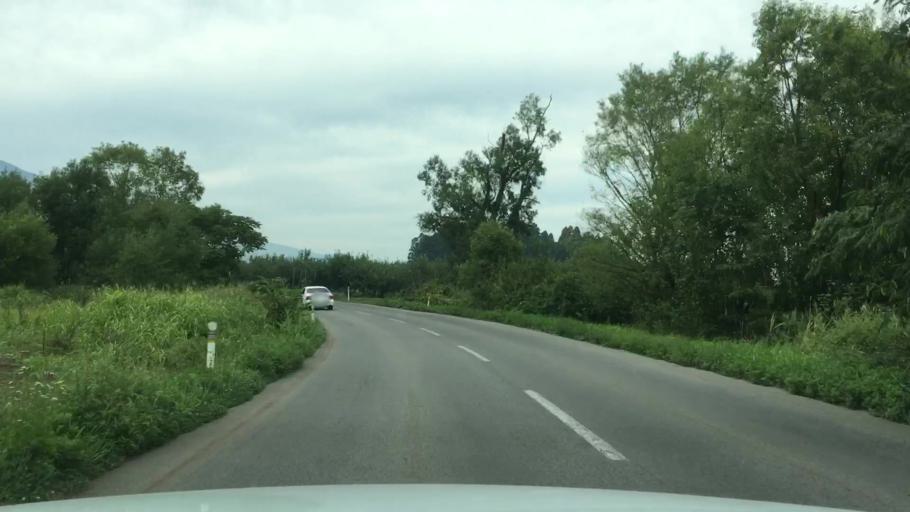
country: JP
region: Aomori
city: Hirosaki
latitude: 40.6431
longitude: 140.4320
